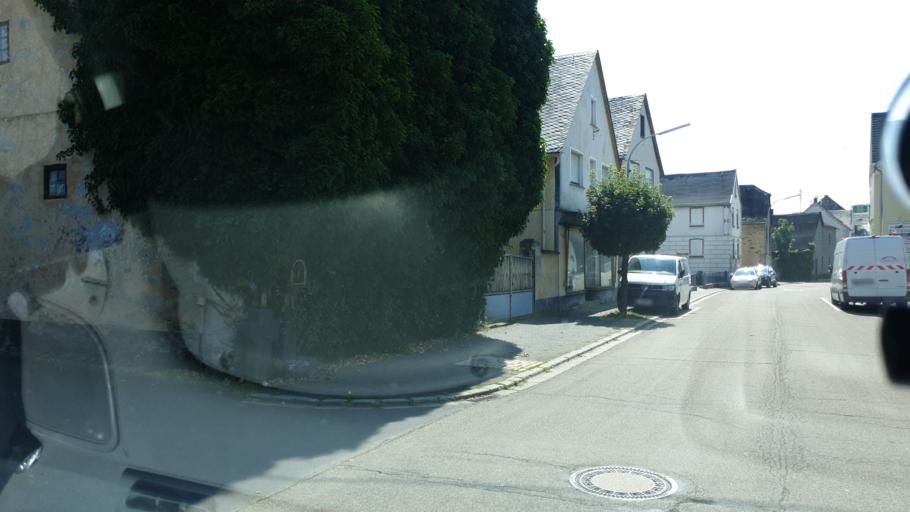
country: DE
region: Rheinland-Pfalz
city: Polch
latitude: 50.2987
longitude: 7.3148
